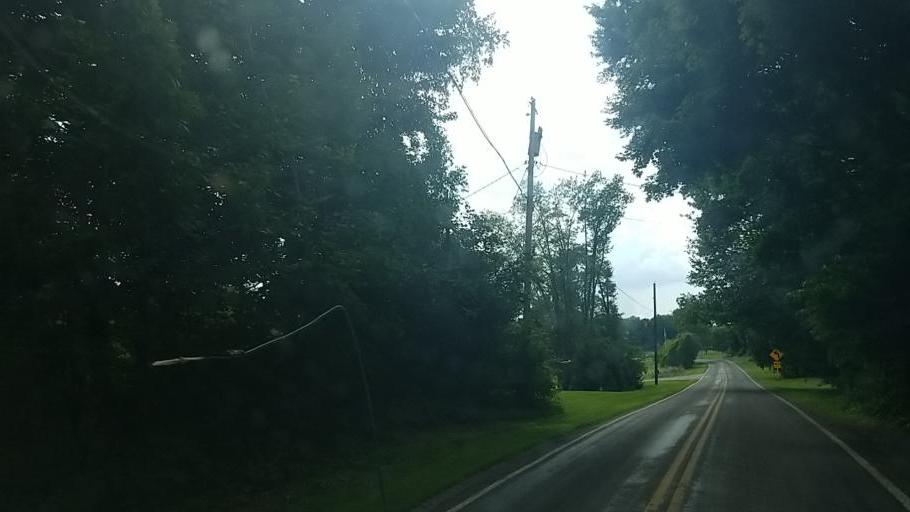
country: US
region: Ohio
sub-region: Wayne County
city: Creston
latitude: 41.0037
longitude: -81.9045
